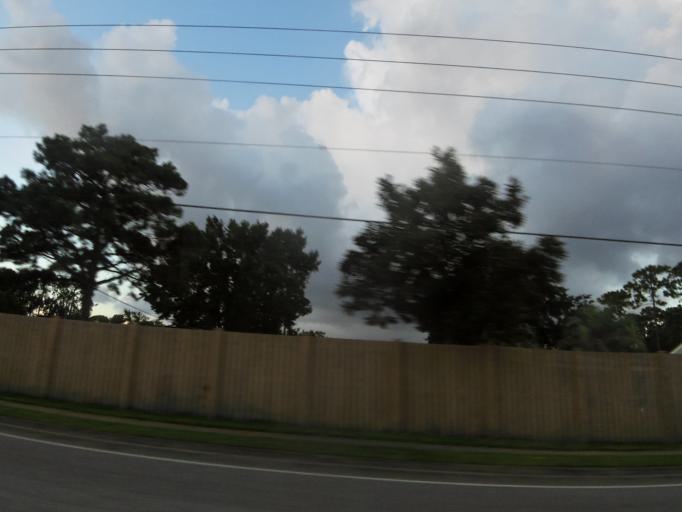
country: US
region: Florida
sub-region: Duval County
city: Jacksonville
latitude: 30.2323
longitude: -81.6005
